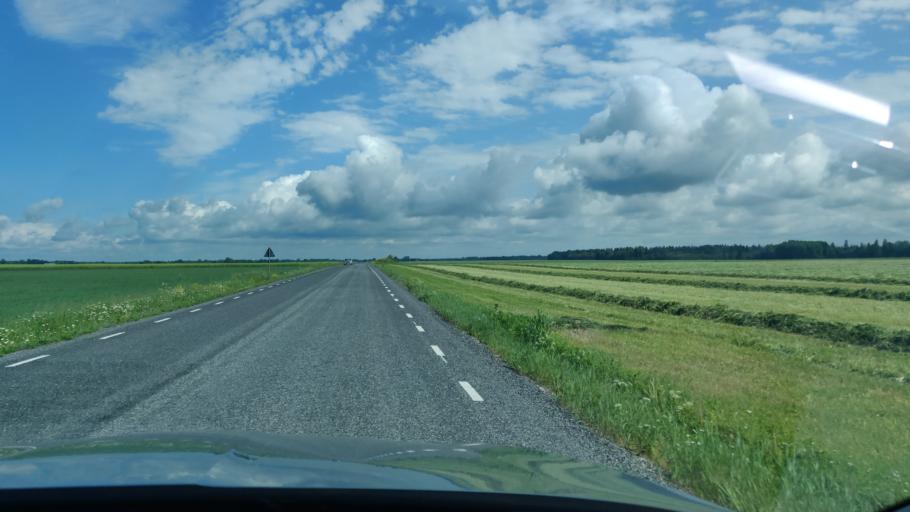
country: EE
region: Jaervamaa
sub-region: Paide linn
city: Paide
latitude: 58.8592
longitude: 25.6622
